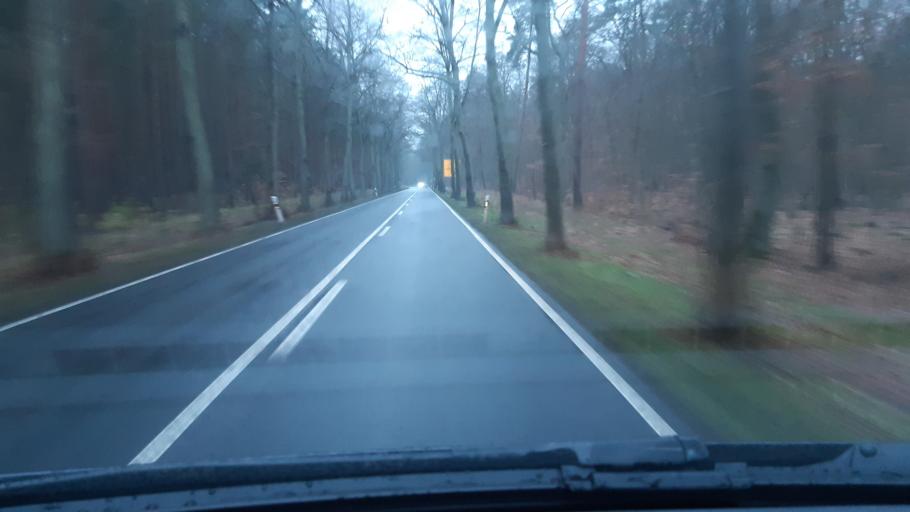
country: DE
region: Brandenburg
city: Templin
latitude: 53.1291
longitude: 13.5412
